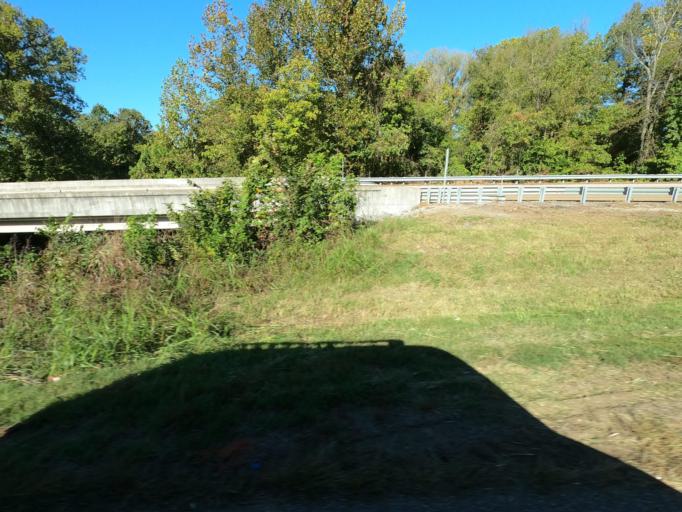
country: US
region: Tennessee
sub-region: Tipton County
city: Brighton
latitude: 35.4971
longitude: -89.7220
